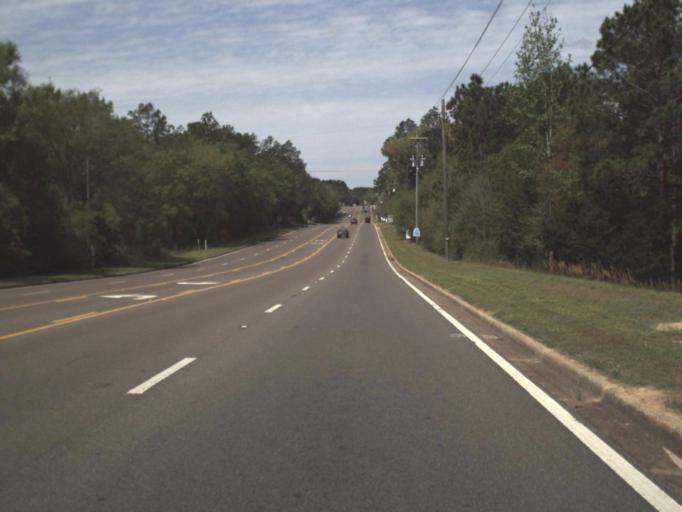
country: US
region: Florida
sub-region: Okaloosa County
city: Crestview
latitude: 30.7608
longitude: -86.5532
